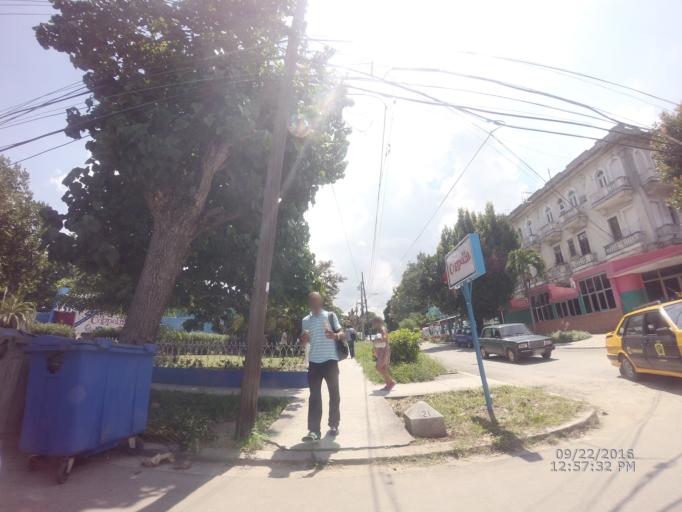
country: CU
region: La Habana
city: Havana
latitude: 23.1400
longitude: -82.3853
